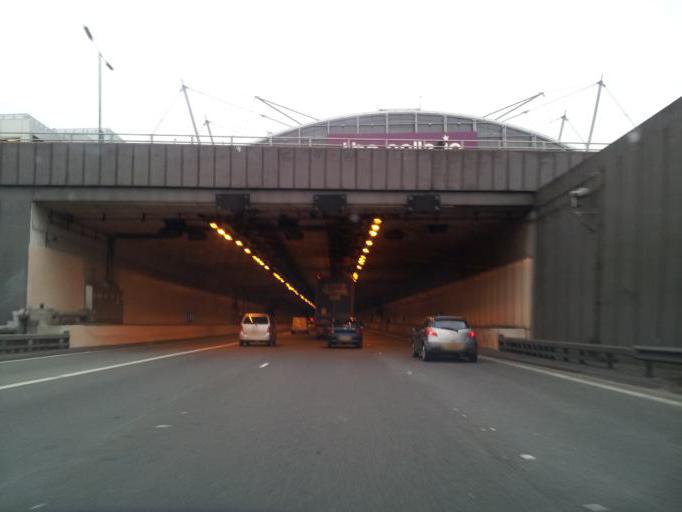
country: GB
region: England
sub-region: Hertfordshire
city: Hatfield
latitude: 51.7601
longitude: -0.2418
